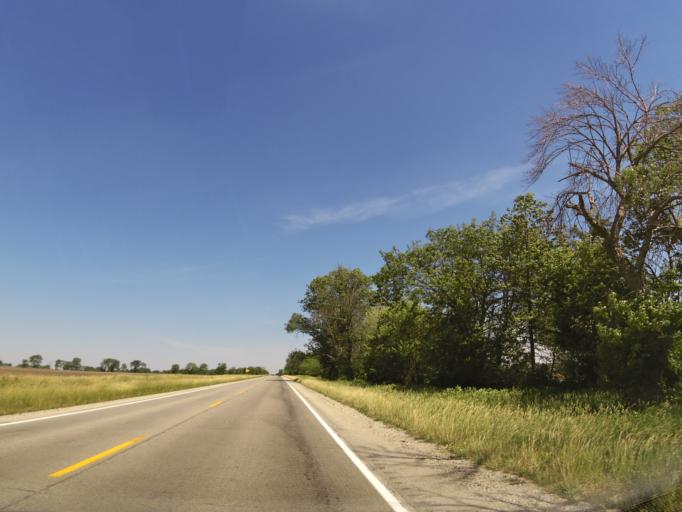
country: US
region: Illinois
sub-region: Vermilion County
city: Danville
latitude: 40.2504
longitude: -87.6471
